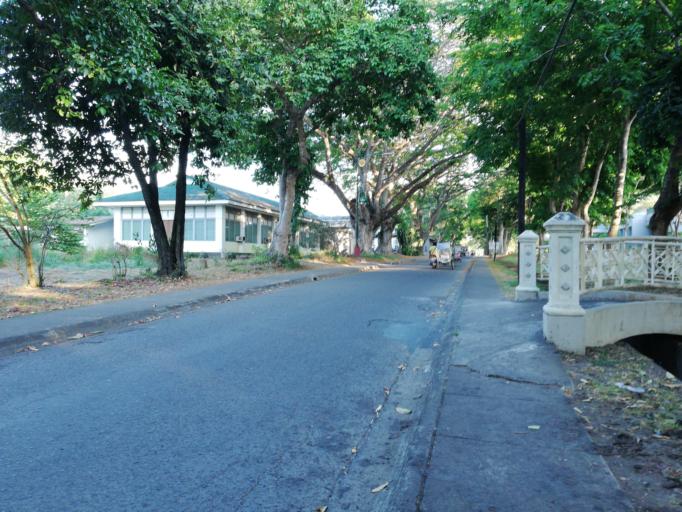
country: PH
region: Calabarzon
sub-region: Province of Laguna
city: Los Banos
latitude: 14.1594
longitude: 121.2439
